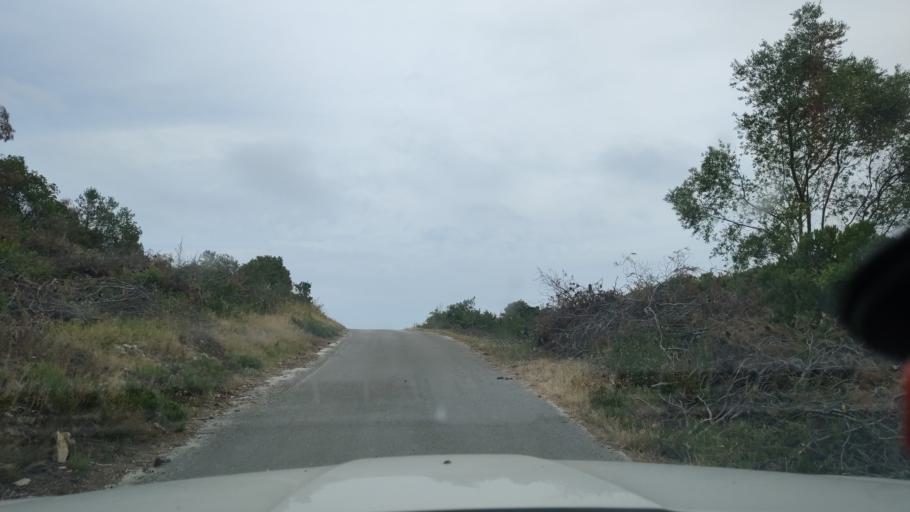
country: HR
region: Splitsko-Dalmatinska
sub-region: Grad Vis
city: Vis
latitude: 43.0285
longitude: 16.1678
